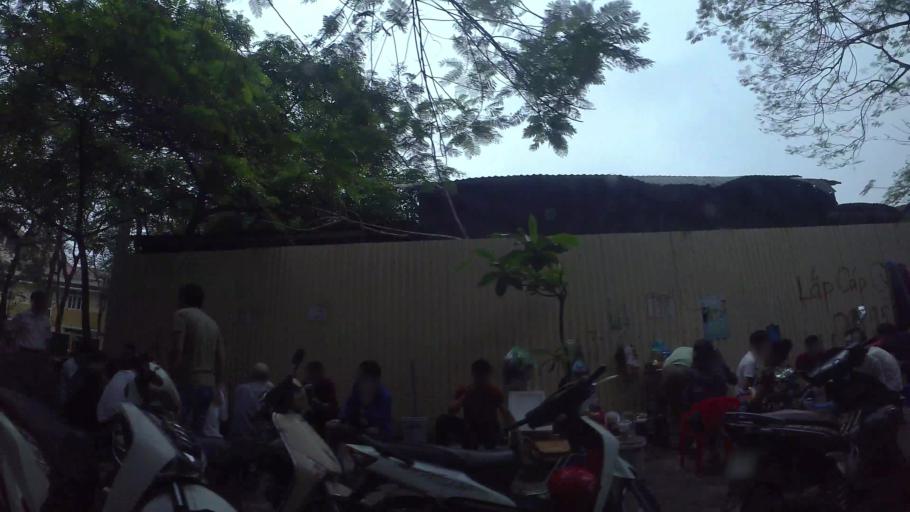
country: VN
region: Ha Noi
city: Hai BaTrung
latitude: 20.9859
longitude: 105.8603
